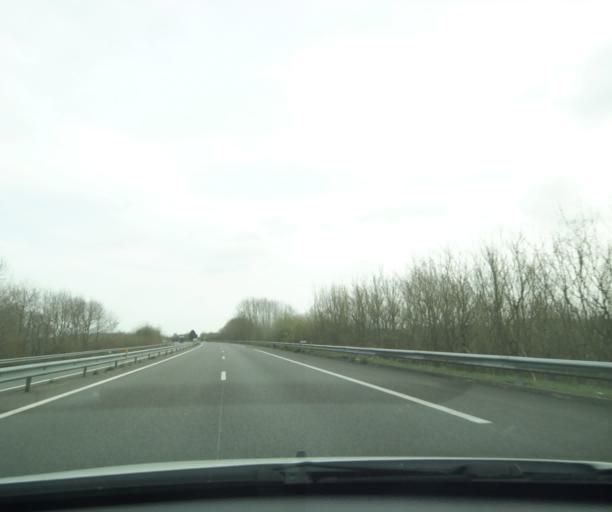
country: FR
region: Aquitaine
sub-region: Departement des Landes
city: Peyrehorade
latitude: 43.5163
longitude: -1.1257
